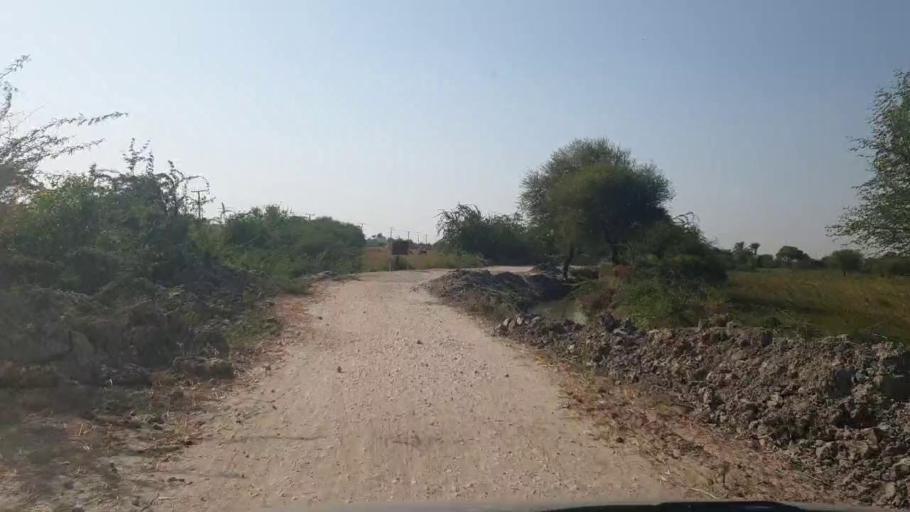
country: PK
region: Sindh
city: Badin
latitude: 24.5796
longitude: 68.7976
